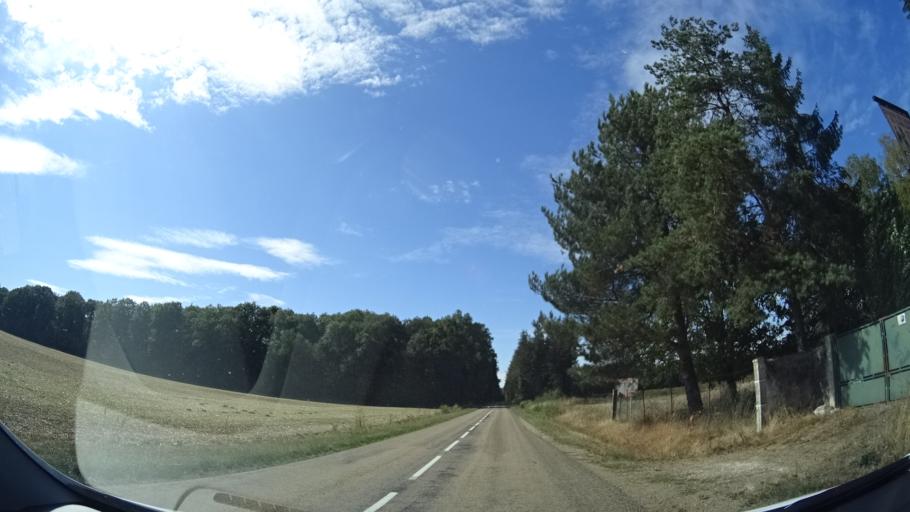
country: FR
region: Bourgogne
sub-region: Departement de l'Yonne
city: Aillant-sur-Tholon
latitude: 47.9232
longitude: 3.2962
